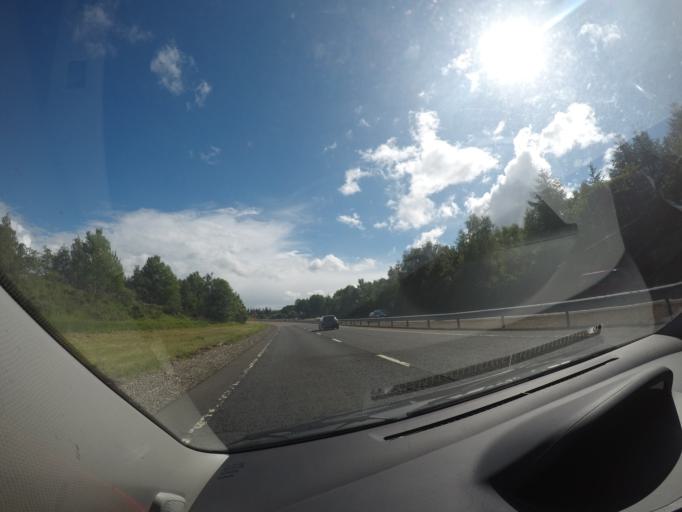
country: GB
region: Scotland
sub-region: Stirling
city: Dunblane
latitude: 56.1903
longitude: -3.9855
